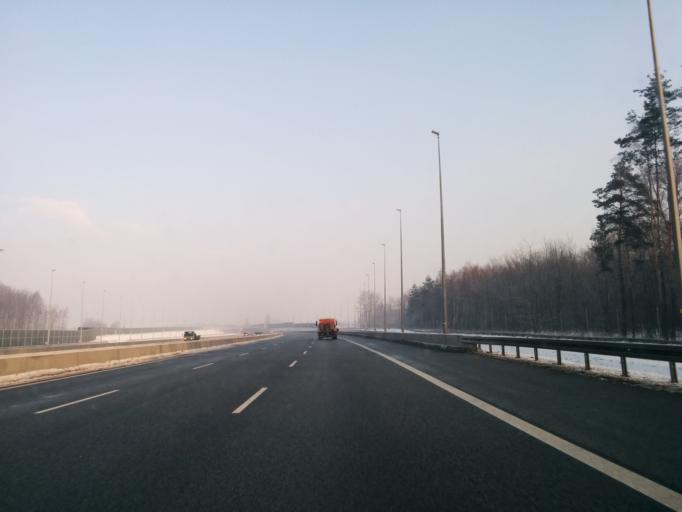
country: PL
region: Silesian Voivodeship
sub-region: Zabrze
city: Zabrze
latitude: 50.3287
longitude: 18.7299
